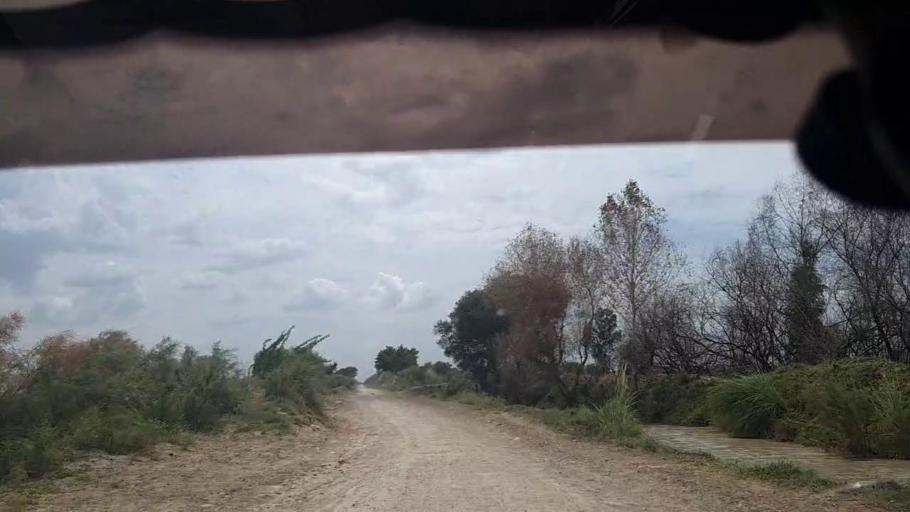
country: PK
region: Sindh
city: Rustam jo Goth
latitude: 28.0372
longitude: 68.9388
